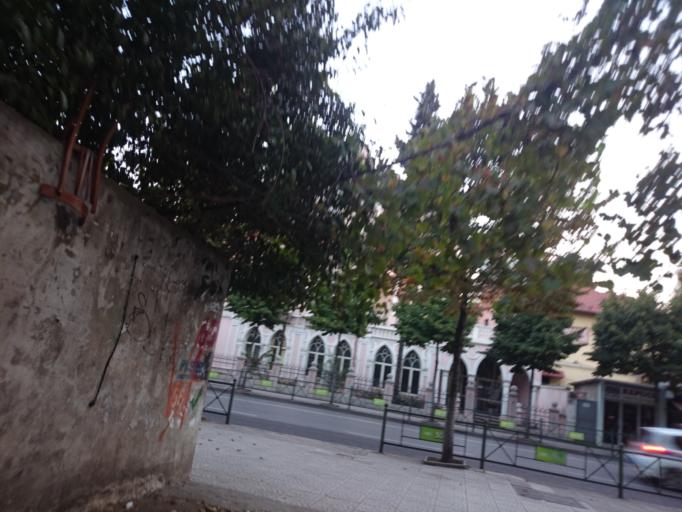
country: AL
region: Tirane
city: Tirana
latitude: 41.3309
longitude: 19.8099
